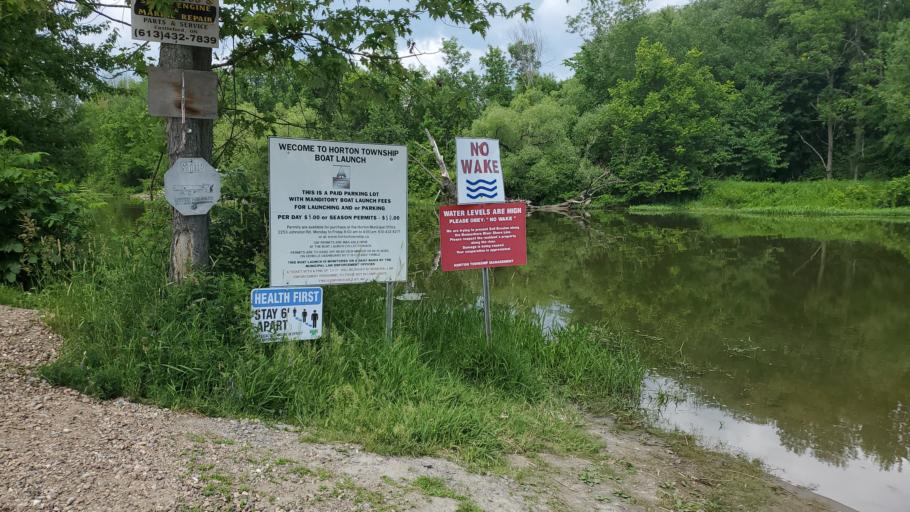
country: CA
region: Quebec
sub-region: Outaouais
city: Shawville
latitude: 45.5145
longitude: -76.5572
